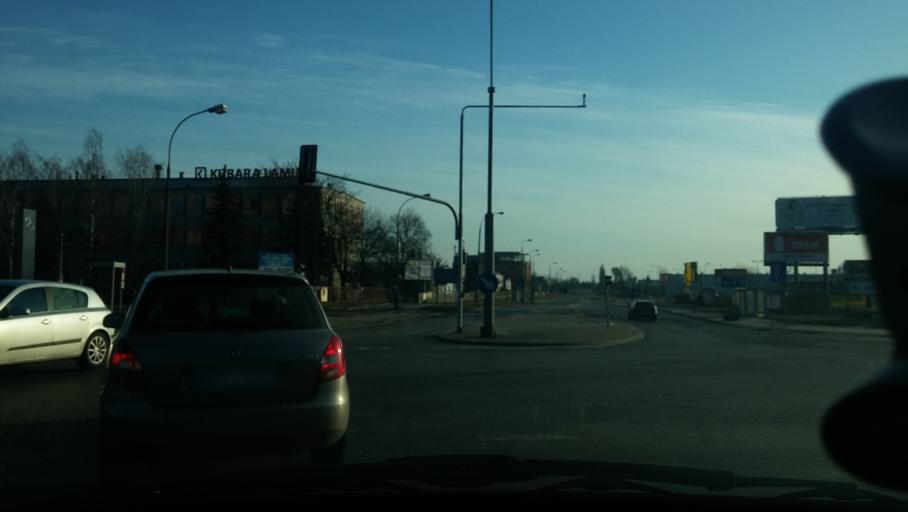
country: PL
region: Masovian Voivodeship
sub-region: Powiat piaseczynski
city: Piaseczno
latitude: 52.0812
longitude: 21.0237
